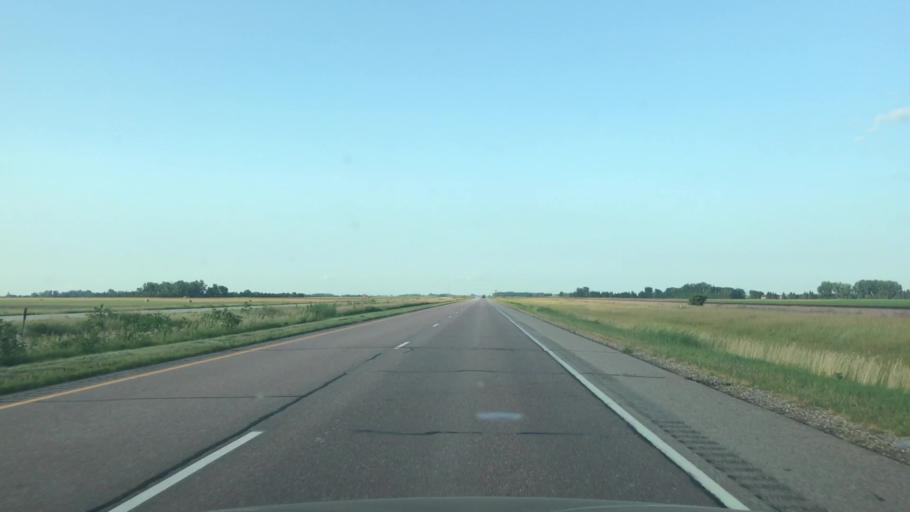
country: US
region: Minnesota
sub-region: Nobles County
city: Worthington
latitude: 43.7384
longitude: -95.4102
